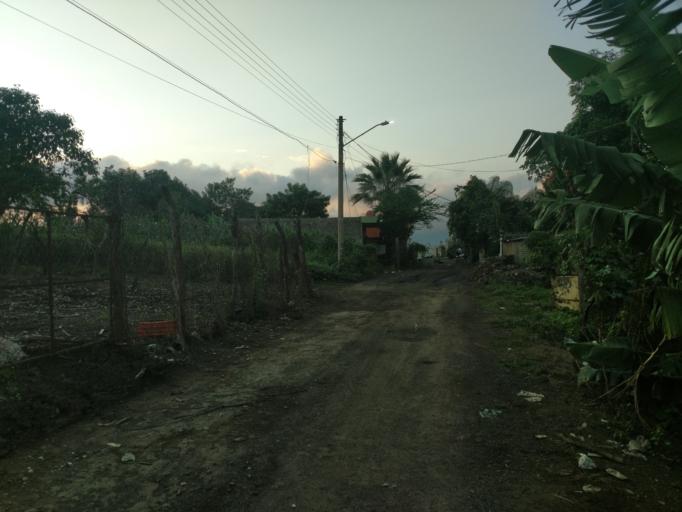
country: MX
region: Nayarit
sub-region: Tepic
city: La Corregidora
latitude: 21.4586
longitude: -104.8009
